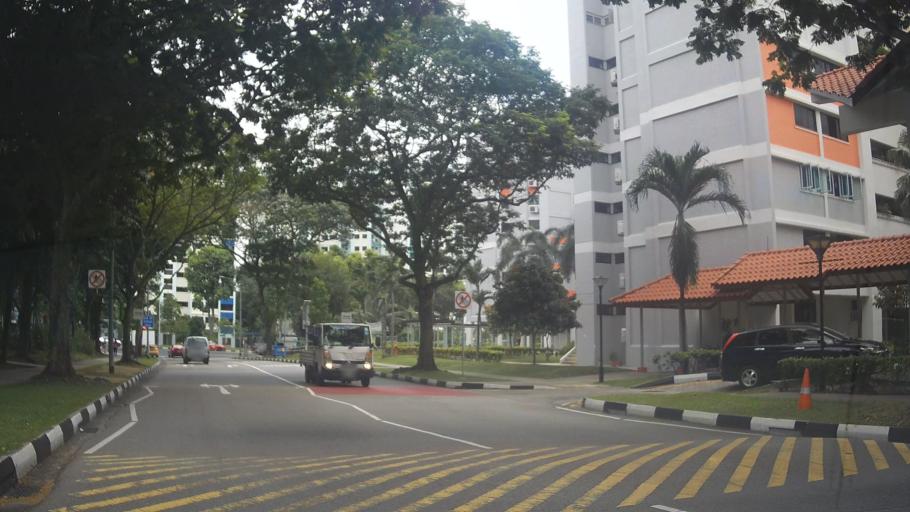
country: SG
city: Singapore
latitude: 1.3568
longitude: 103.8715
